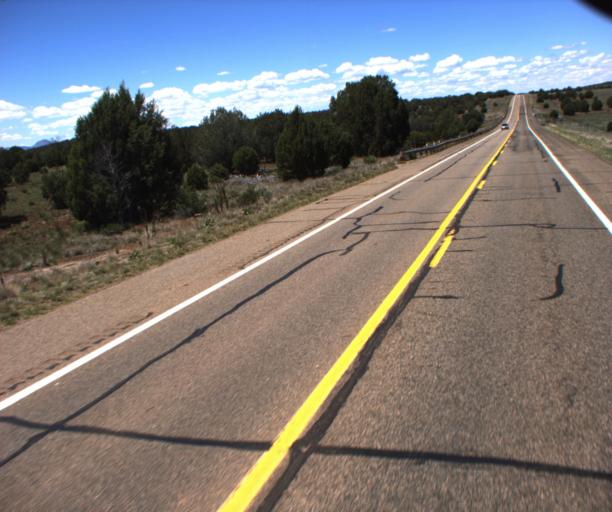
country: US
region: Arizona
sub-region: Yavapai County
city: Paulden
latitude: 35.1397
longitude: -112.4431
